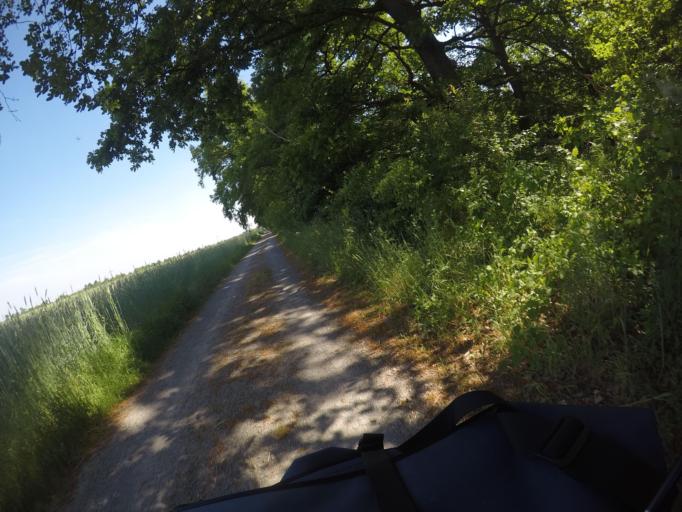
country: DE
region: Baden-Wuerttemberg
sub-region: Karlsruhe Region
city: Rheinstetten
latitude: 48.9479
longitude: 8.3184
